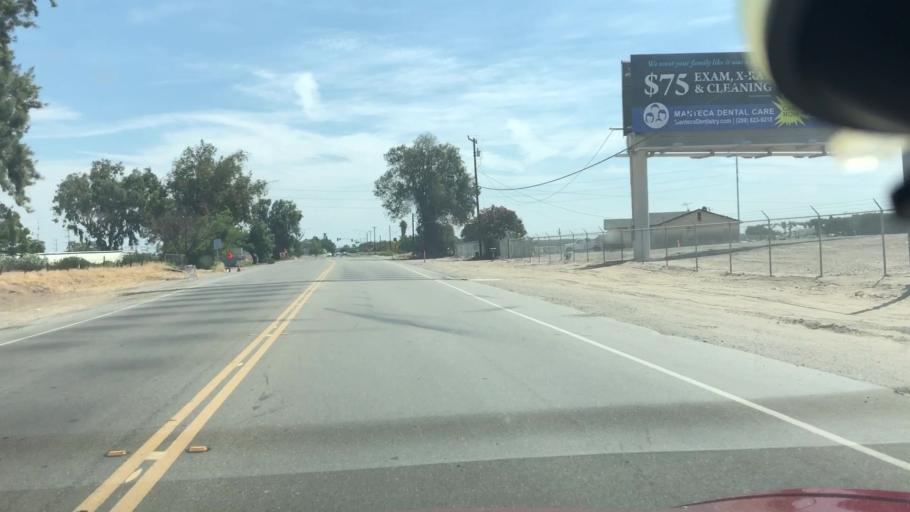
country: US
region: California
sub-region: San Joaquin County
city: Lathrop
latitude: 37.7941
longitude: -121.2819
